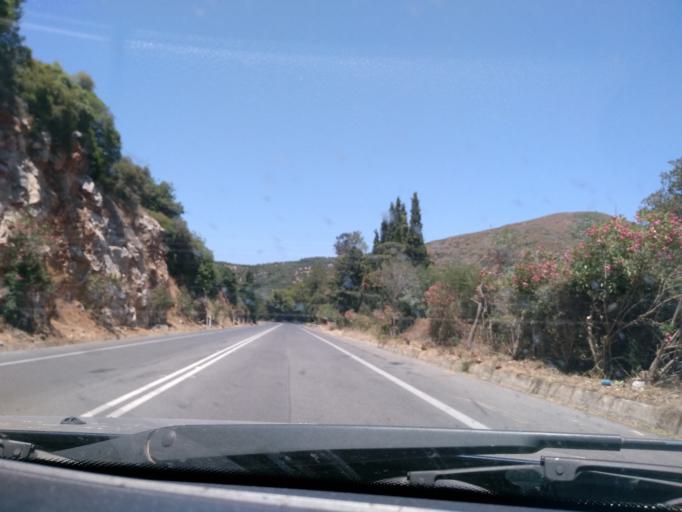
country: GR
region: Crete
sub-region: Nomos Rethymnis
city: Anogeia
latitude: 35.3951
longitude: 24.8783
